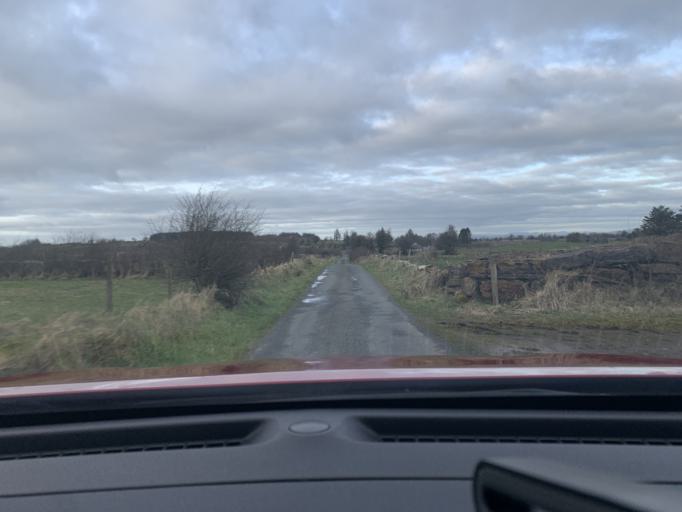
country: IE
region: Connaught
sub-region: Roscommon
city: Ballaghaderreen
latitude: 53.9692
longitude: -8.5593
